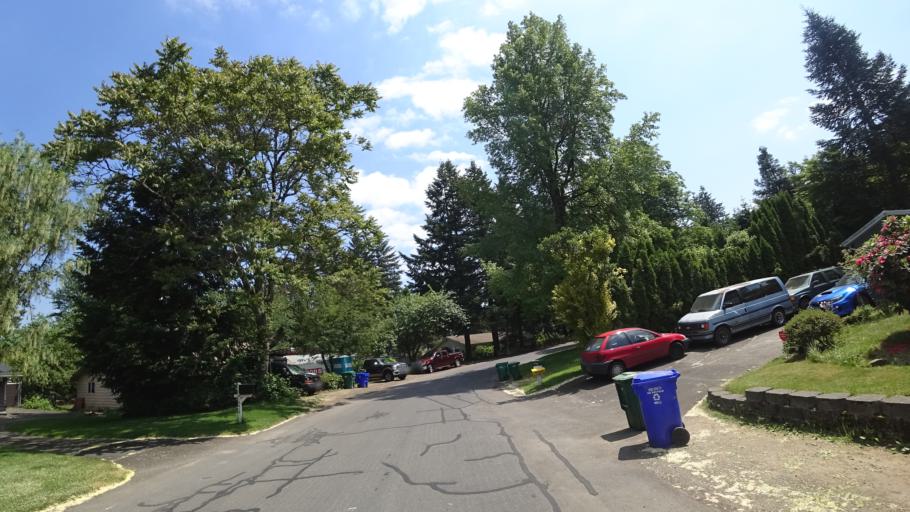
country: US
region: Oregon
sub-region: Multnomah County
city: Fairview
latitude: 45.5326
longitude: -122.4938
